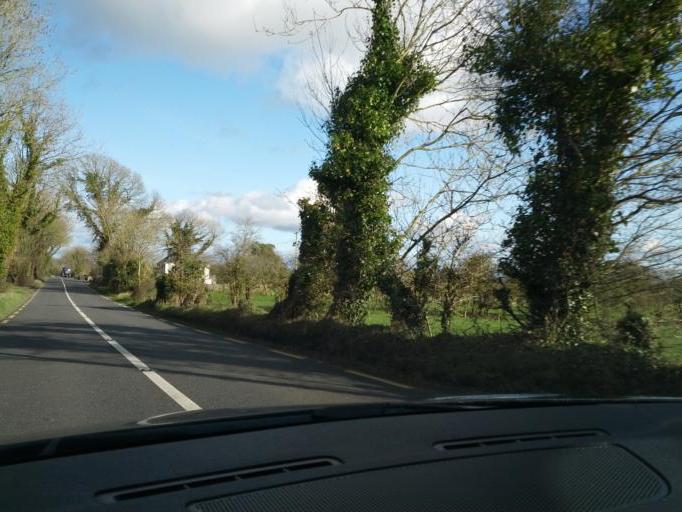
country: IE
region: Connaught
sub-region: Roscommon
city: Roscommon
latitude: 53.6632
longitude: -8.2897
